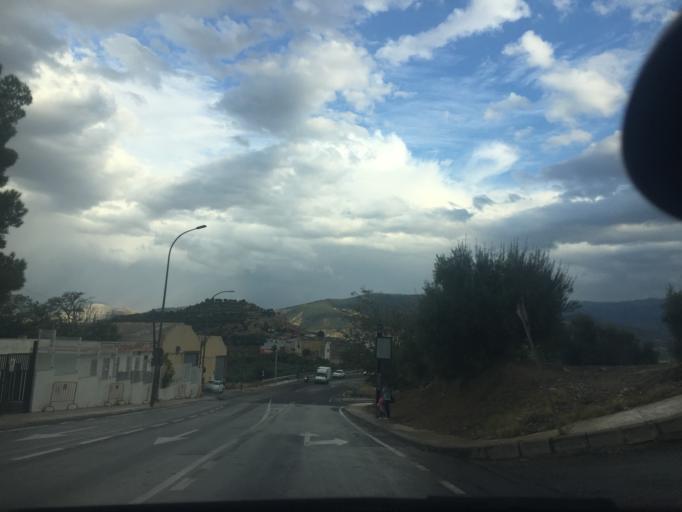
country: ES
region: Andalusia
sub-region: Provincia de Jaen
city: Jaen
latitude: 37.7676
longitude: -3.7761
